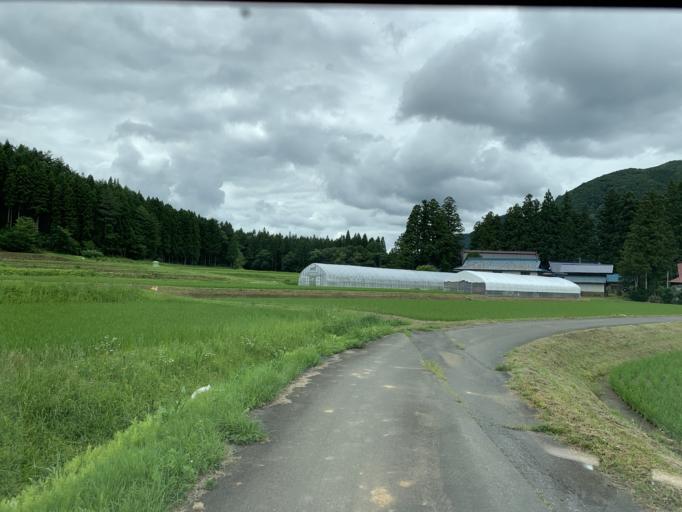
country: JP
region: Iwate
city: Ichinoseki
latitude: 38.9795
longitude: 140.9122
